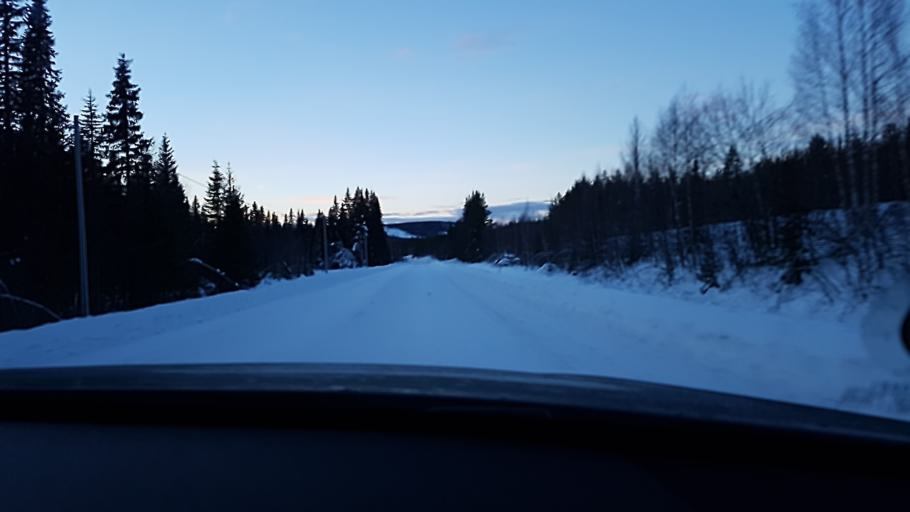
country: SE
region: Vaesterbotten
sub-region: Sorsele Kommun
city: Sorsele
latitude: 65.1842
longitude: 17.4772
